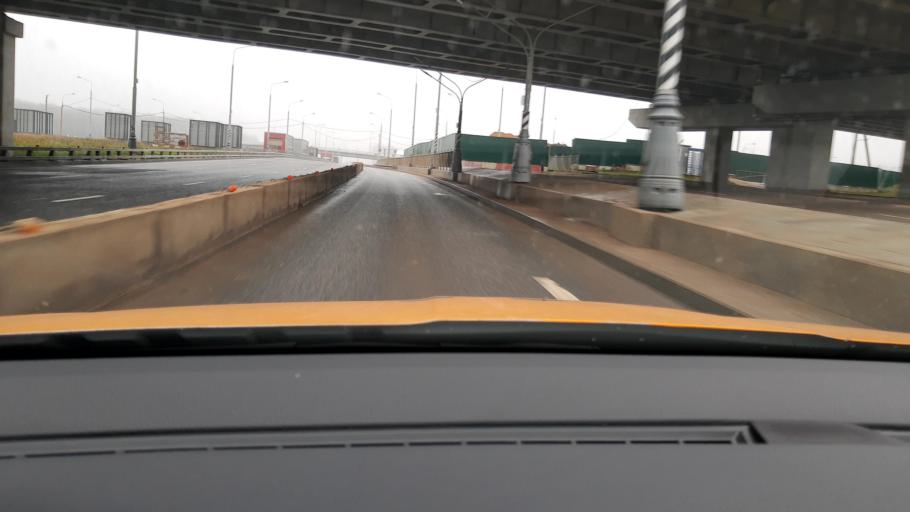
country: RU
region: Moskovskaya
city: Kommunarka
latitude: 55.5621
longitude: 37.4653
